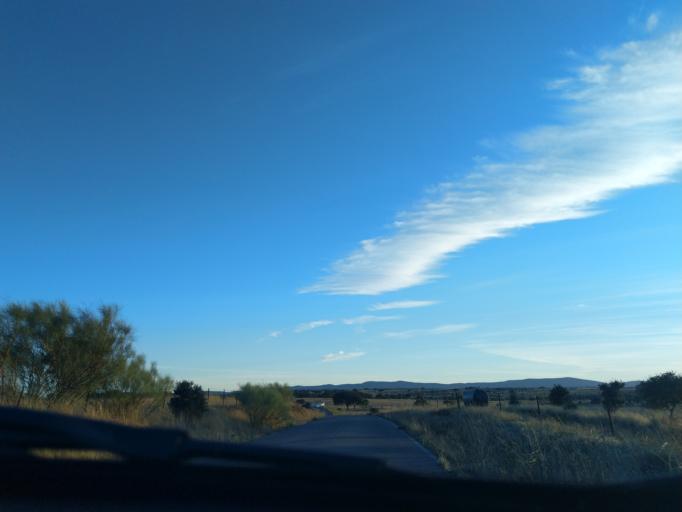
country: ES
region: Extremadura
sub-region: Provincia de Badajoz
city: Ahillones
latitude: 38.2484
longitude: -5.8255
